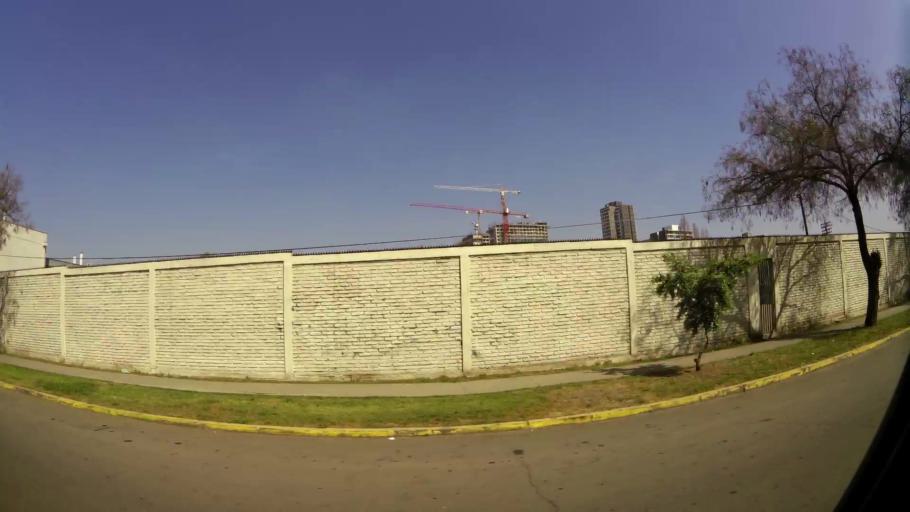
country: CL
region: Santiago Metropolitan
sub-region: Provincia de Santiago
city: Lo Prado
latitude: -33.4494
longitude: -70.6896
